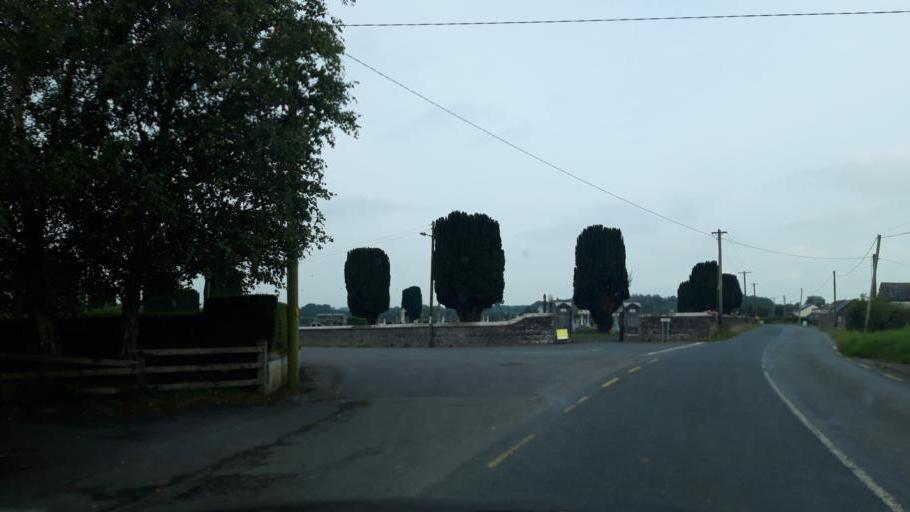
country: IE
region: Leinster
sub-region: Kilkenny
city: Callan
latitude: 52.5316
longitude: -7.4101
